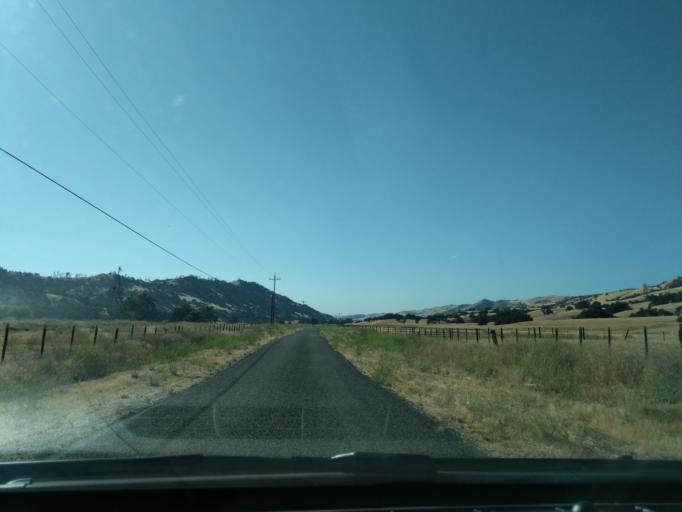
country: US
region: California
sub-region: San Luis Obispo County
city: San Miguel
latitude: 36.1195
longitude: -120.7318
